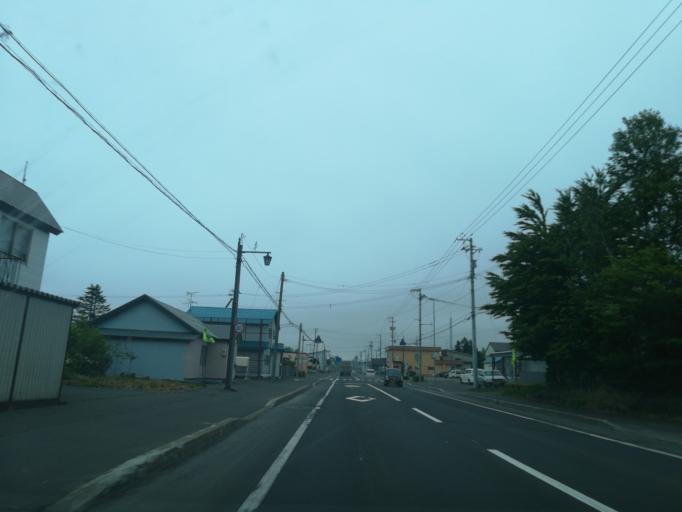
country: JP
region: Hokkaido
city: Ebetsu
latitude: 43.0705
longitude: 141.6487
